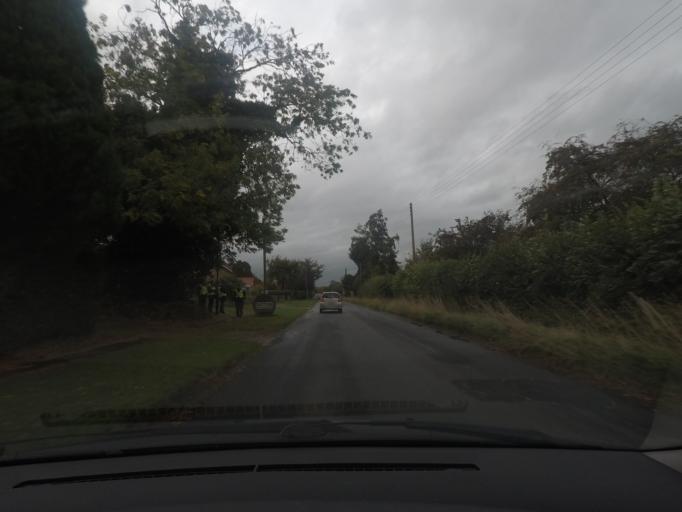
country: GB
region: England
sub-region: City of York
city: Wigginton
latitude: 54.0740
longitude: -1.1006
